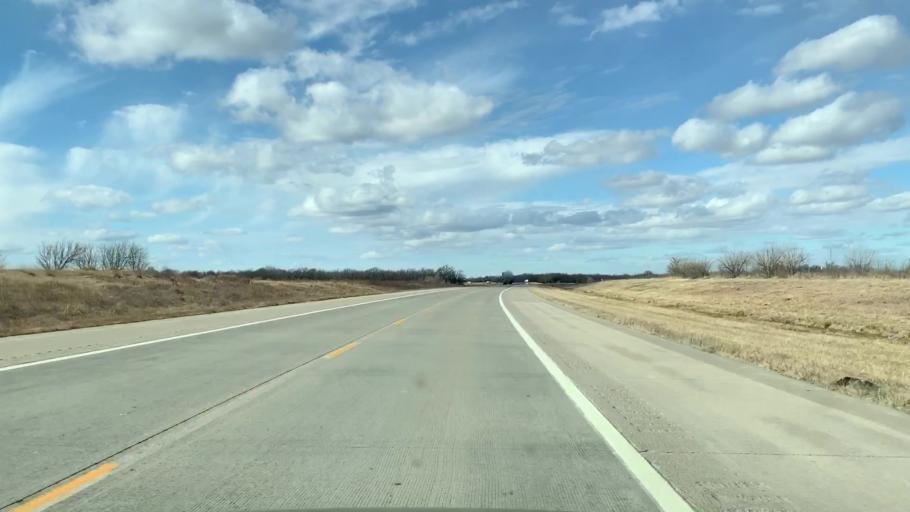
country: US
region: Kansas
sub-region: Labette County
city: Parsons
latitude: 37.3538
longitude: -95.2116
